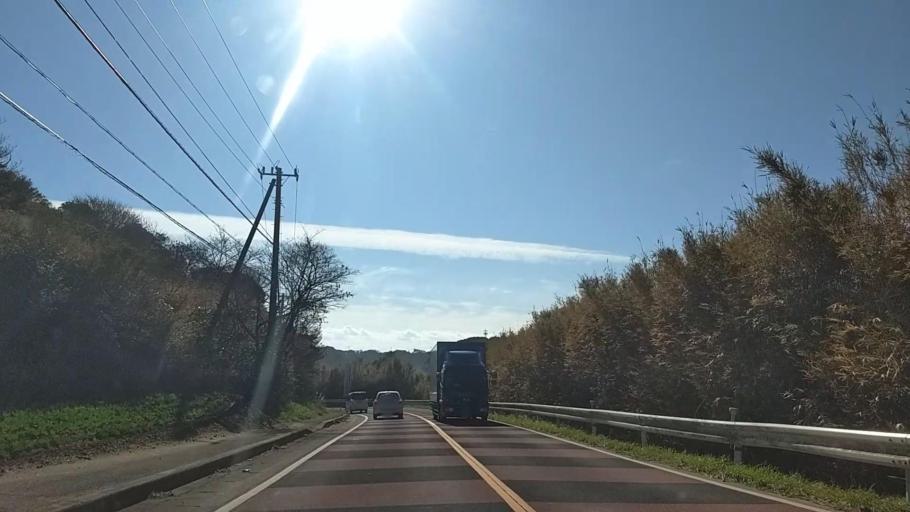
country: JP
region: Chiba
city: Asahi
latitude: 35.7048
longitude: 140.7407
